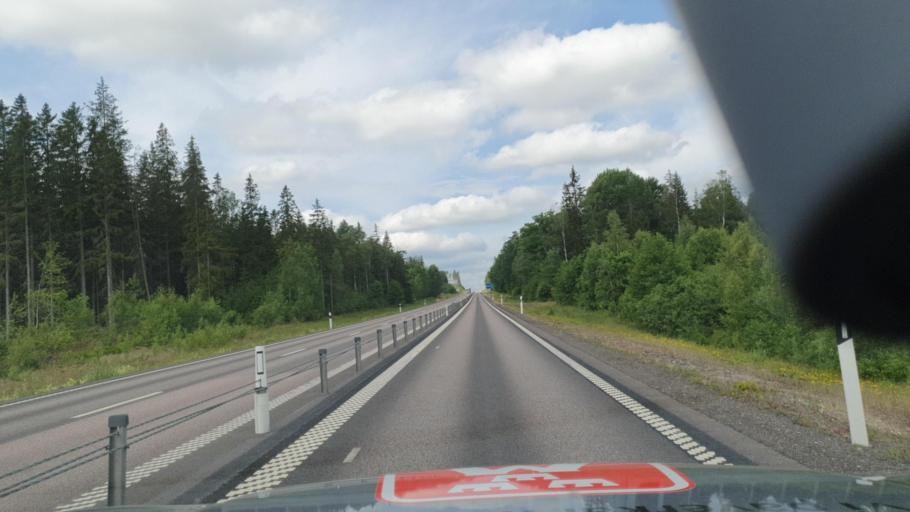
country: SE
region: Kalmar
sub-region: Emmaboda Kommun
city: Emmaboda
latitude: 56.7199
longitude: 15.6360
